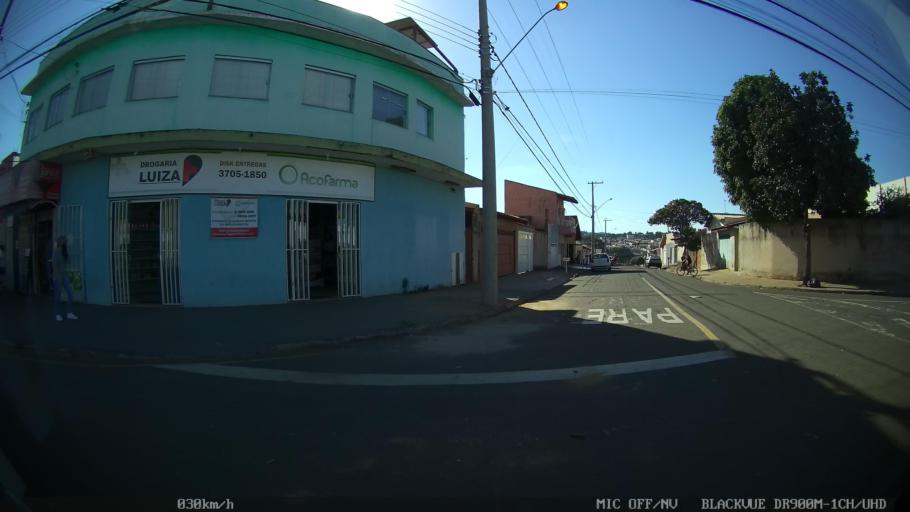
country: BR
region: Sao Paulo
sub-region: Franca
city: Franca
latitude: -20.4886
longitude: -47.4226
